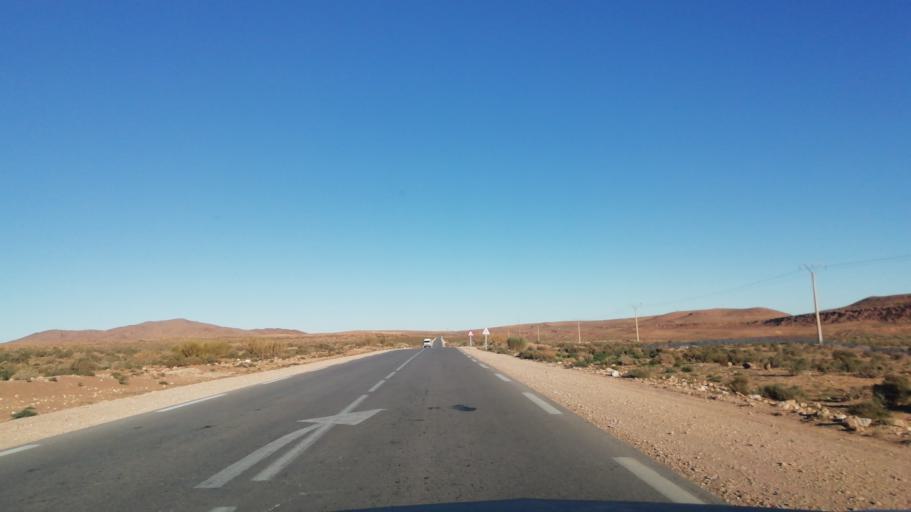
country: DZ
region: El Bayadh
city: El Abiodh Sidi Cheikh
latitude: 33.1649
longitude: 0.4130
